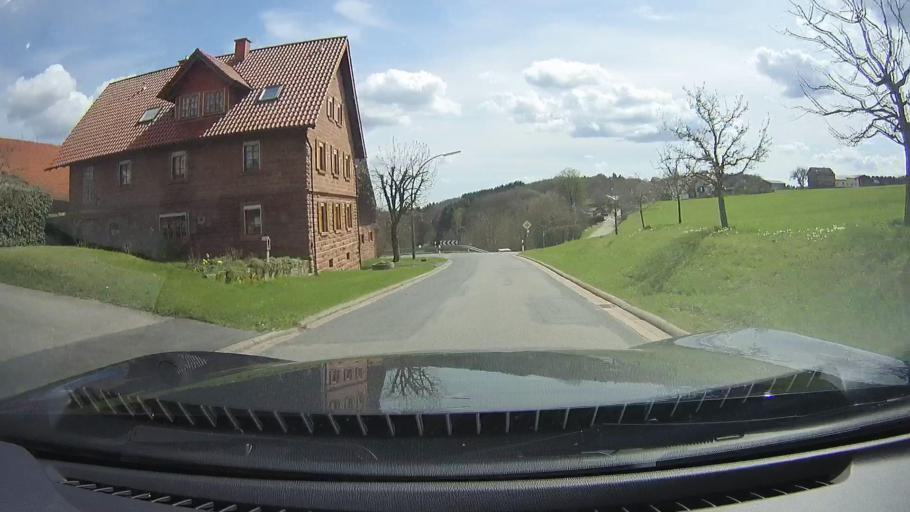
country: DE
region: Bavaria
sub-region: Regierungsbezirk Unterfranken
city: Kirchzell
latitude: 49.6198
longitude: 9.1104
